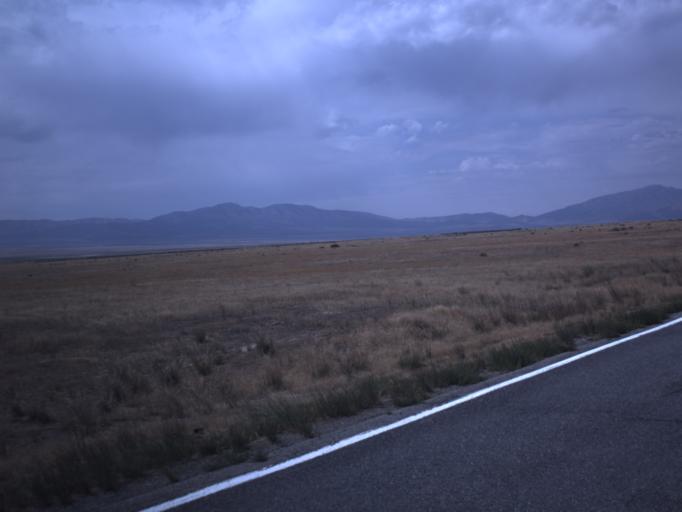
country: US
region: Utah
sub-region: Utah County
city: Eagle Mountain
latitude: 40.2444
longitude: -112.2099
